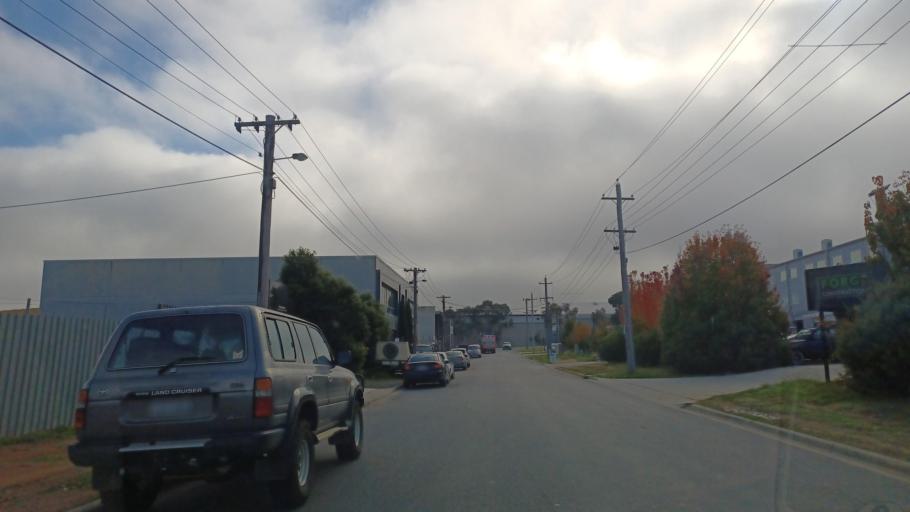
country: AU
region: Australian Capital Territory
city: Kaleen
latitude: -35.2174
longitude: 149.1440
